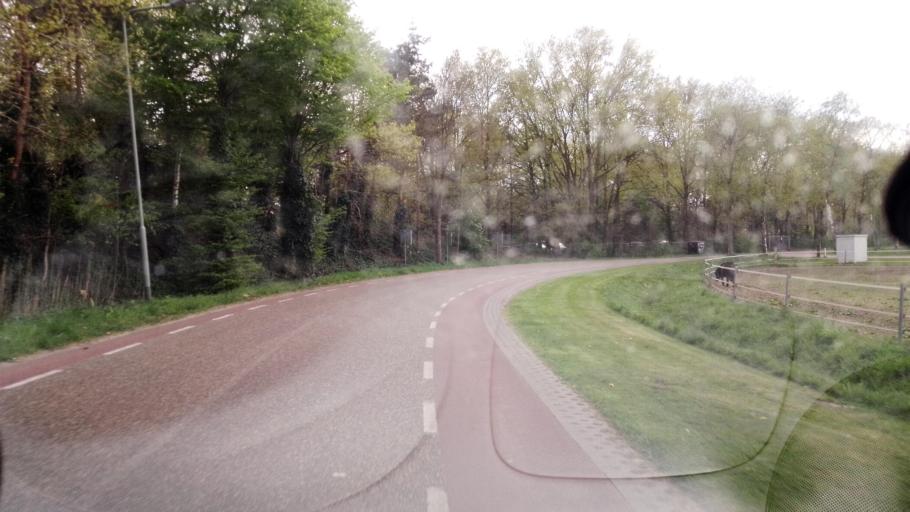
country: NL
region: Limburg
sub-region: Gemeente Venray
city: Venray
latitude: 51.4587
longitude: 5.9500
